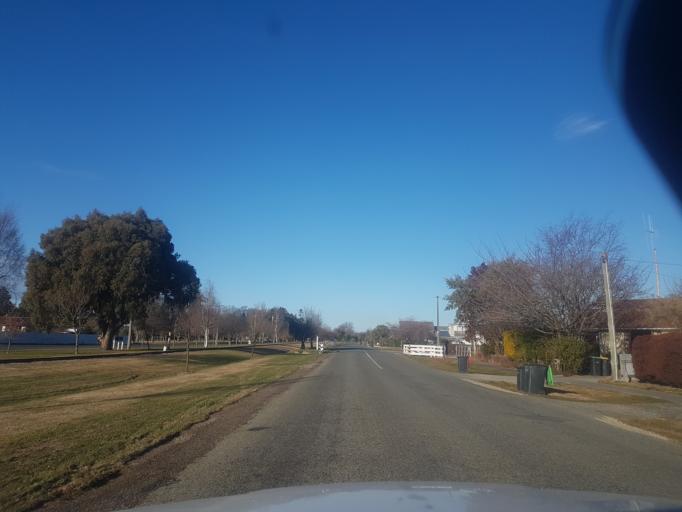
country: NZ
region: Canterbury
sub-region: Timaru District
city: Pleasant Point
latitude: -44.2634
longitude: 171.1376
